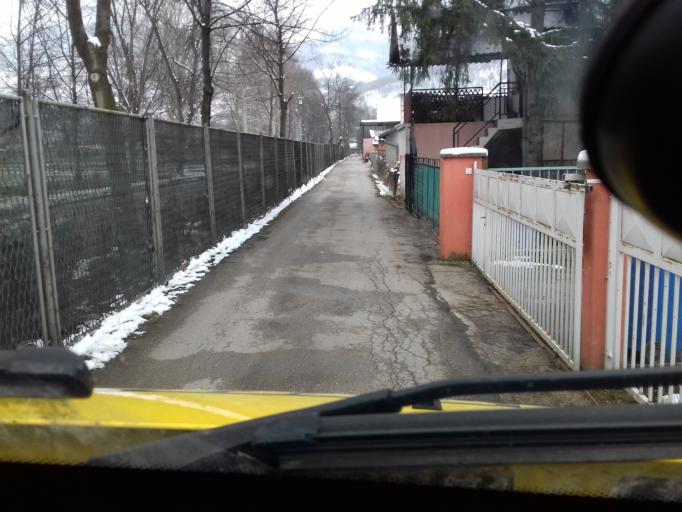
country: BA
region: Federation of Bosnia and Herzegovina
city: Zenica
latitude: 44.1934
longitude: 17.9239
